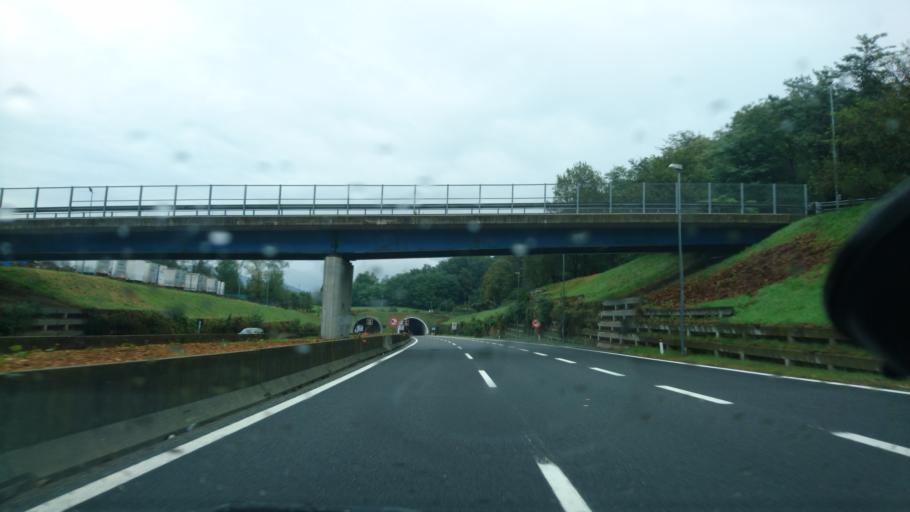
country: IT
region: Piedmont
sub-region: Provincia di Novara
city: Colazza
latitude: 45.7784
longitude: 8.5065
